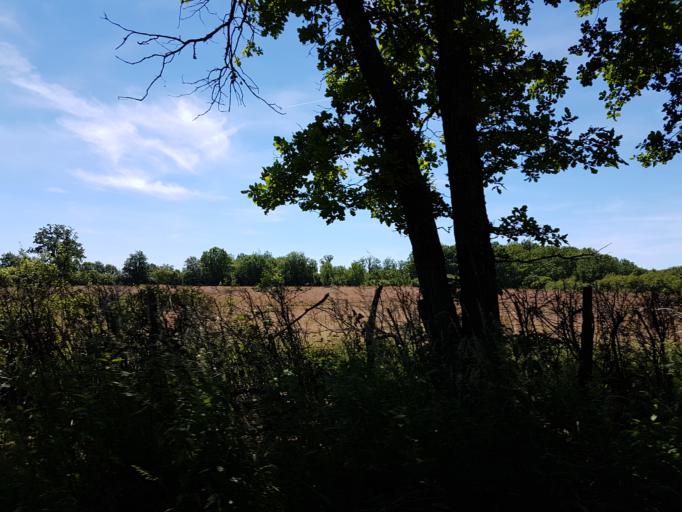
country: FR
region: Bourgogne
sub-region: Departement de Saone-et-Loire
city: Epinac
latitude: 46.9891
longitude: 4.4956
